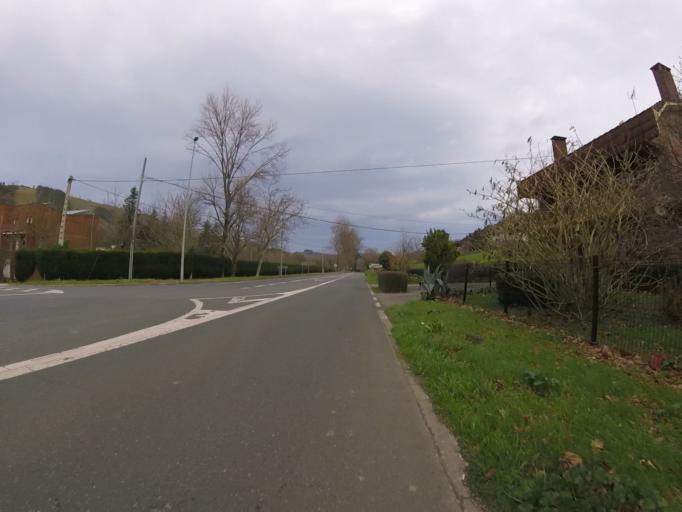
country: ES
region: Basque Country
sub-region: Provincia de Guipuzcoa
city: Aizarnazabal
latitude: 43.2629
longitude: -2.2375
